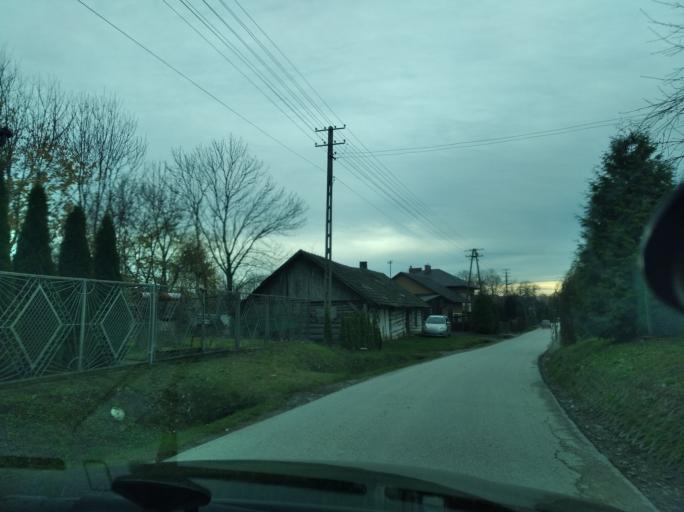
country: PL
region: Subcarpathian Voivodeship
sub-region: Powiat przeworski
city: Debow
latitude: 50.0466
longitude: 22.4512
